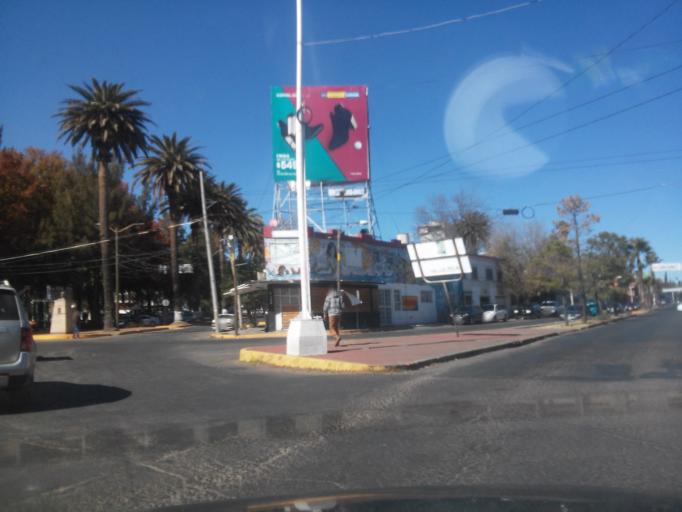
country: MX
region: Durango
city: Victoria de Durango
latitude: 24.0221
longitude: -104.6771
